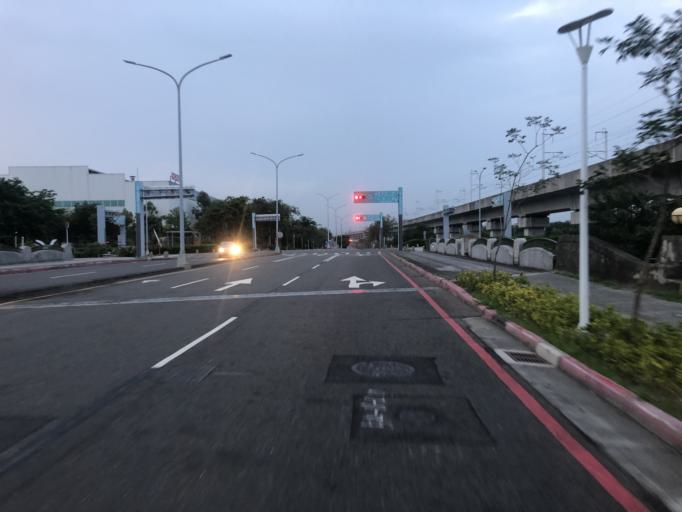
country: TW
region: Taiwan
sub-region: Tainan
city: Tainan
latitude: 23.0901
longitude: 120.2863
